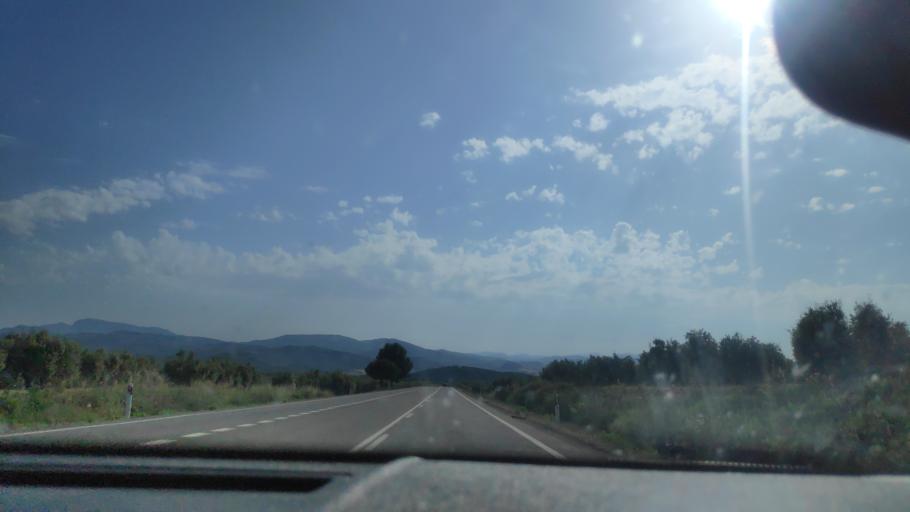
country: ES
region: Andalusia
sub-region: Provincia de Jaen
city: Frailes
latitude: 37.4304
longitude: -3.7849
